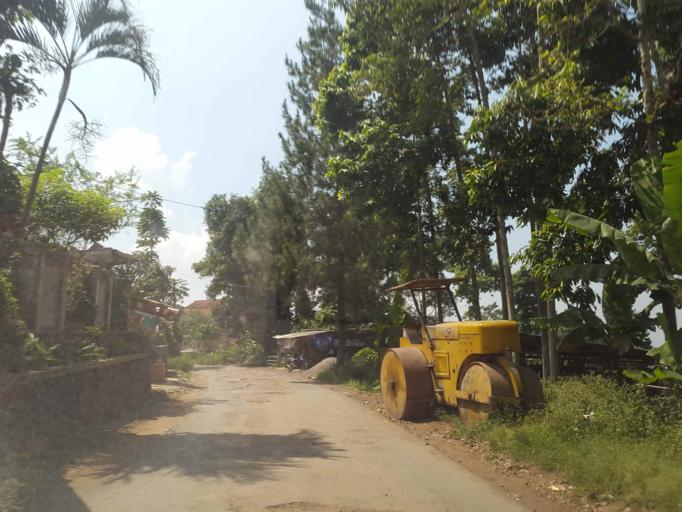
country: ID
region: West Java
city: Sukabumi
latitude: -6.8092
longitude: 107.0586
